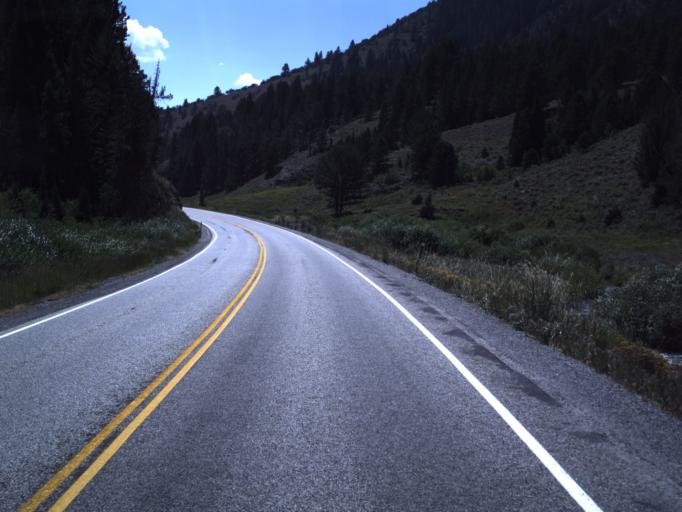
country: US
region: Utah
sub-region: Cache County
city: Richmond
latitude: 41.9578
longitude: -111.5400
